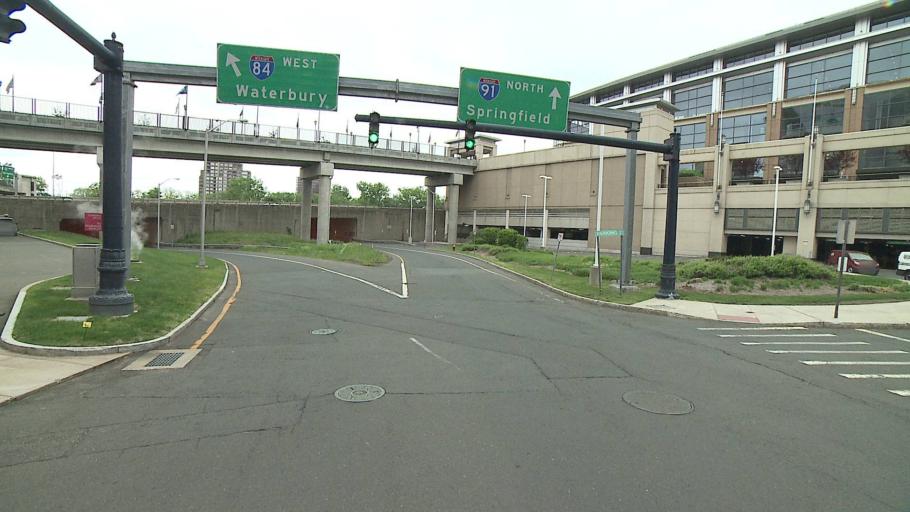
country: US
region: Connecticut
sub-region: Hartford County
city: Hartford
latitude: 41.7642
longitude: -72.6689
